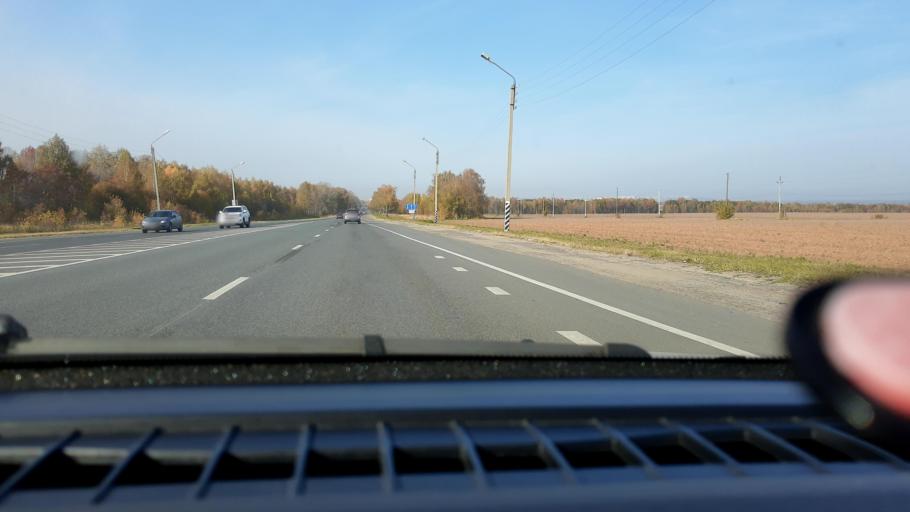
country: RU
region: Nizjnij Novgorod
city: Kstovo
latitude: 56.1321
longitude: 44.2498
